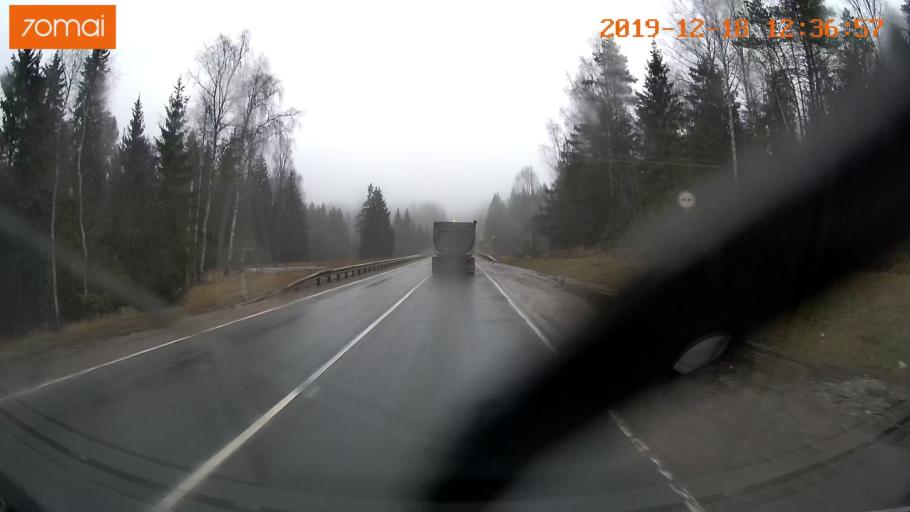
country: RU
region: Moskovskaya
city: Rumyantsevo
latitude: 56.1409
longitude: 36.5980
